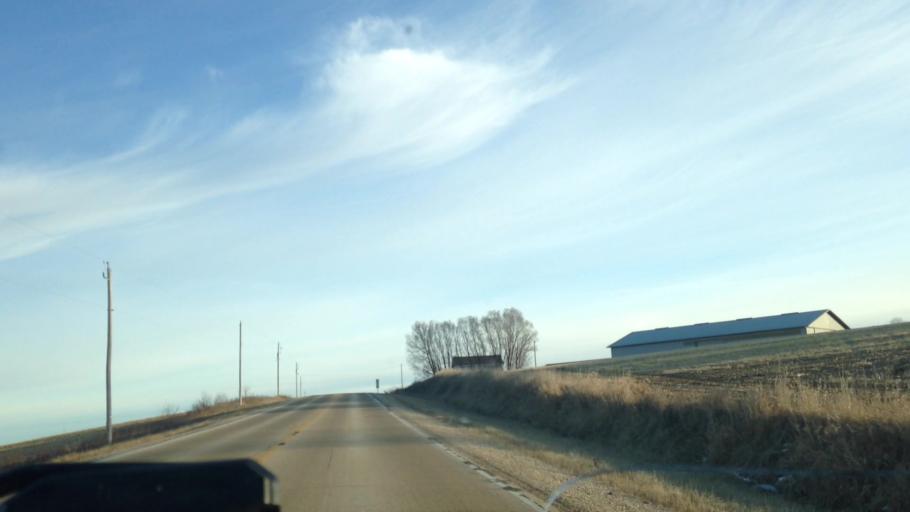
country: US
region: Wisconsin
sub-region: Dodge County
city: Mayville
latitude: 43.5252
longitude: -88.5080
